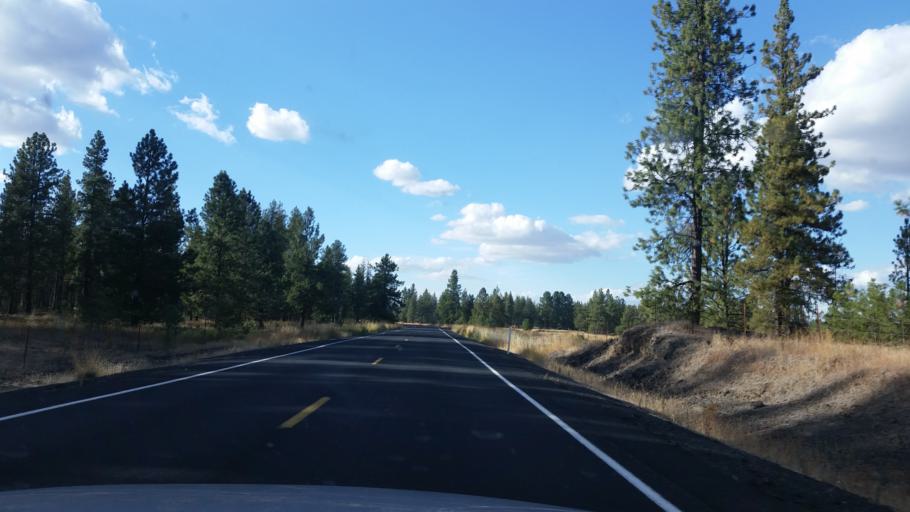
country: US
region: Washington
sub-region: Spokane County
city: Cheney
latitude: 47.4325
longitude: -117.5681
